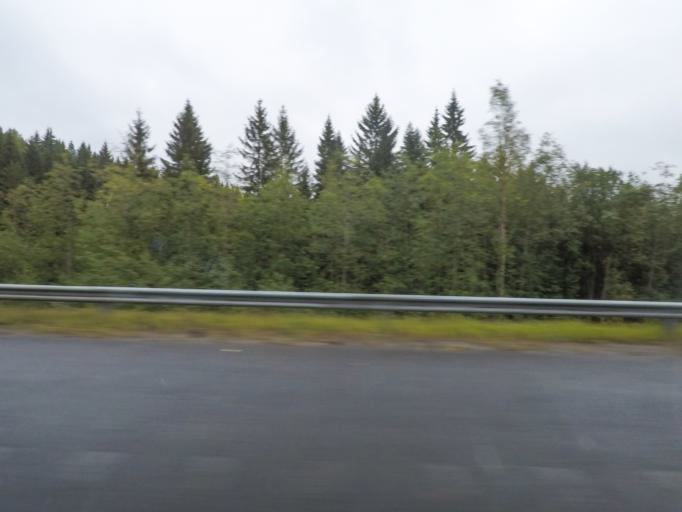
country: FI
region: Northern Savo
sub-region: Kuopio
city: Kuopio
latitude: 62.8516
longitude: 27.6210
